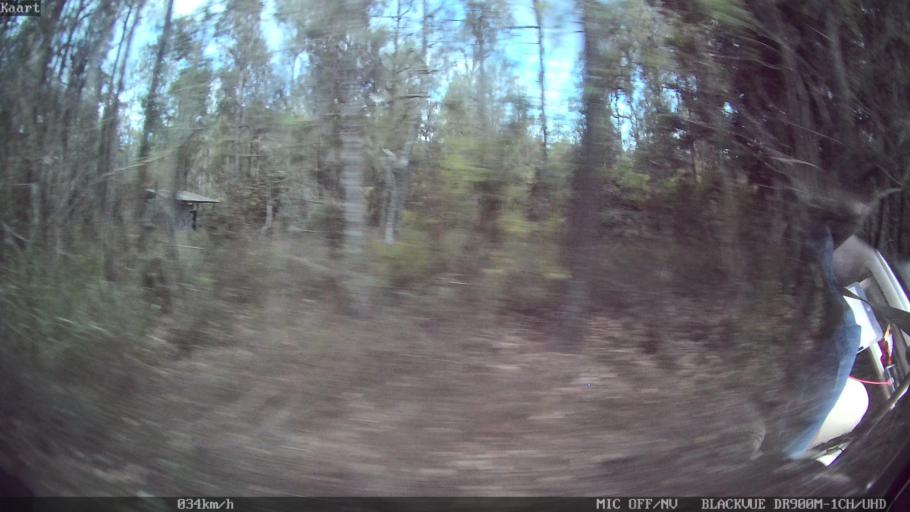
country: ID
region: Bali
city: Banjar Kedisan
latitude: -8.2342
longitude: 115.3564
